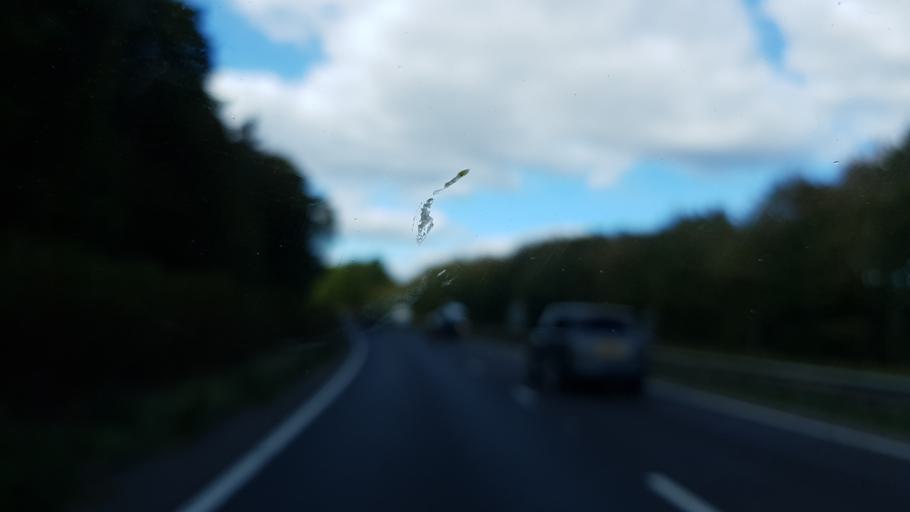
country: GB
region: England
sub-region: Surrey
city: Milford
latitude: 51.1987
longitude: -0.6461
